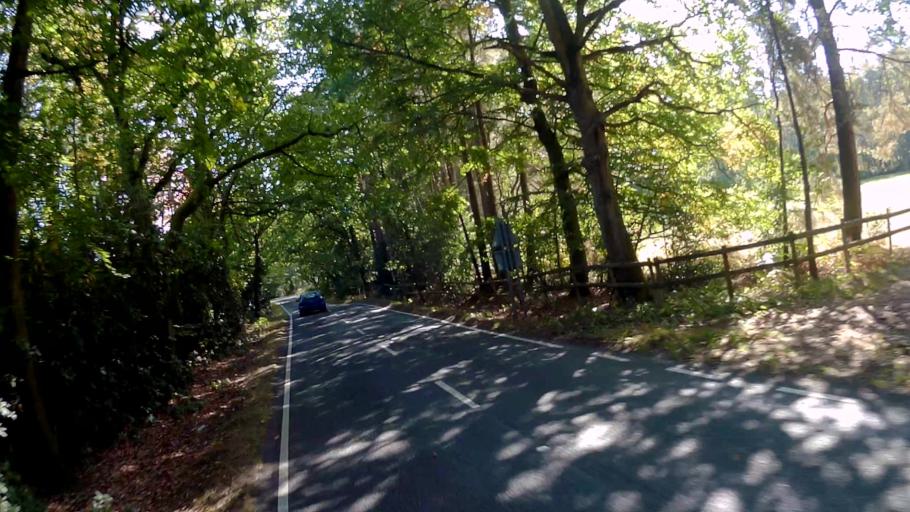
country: GB
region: England
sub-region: Surrey
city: Farnham
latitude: 51.1938
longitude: -0.7712
